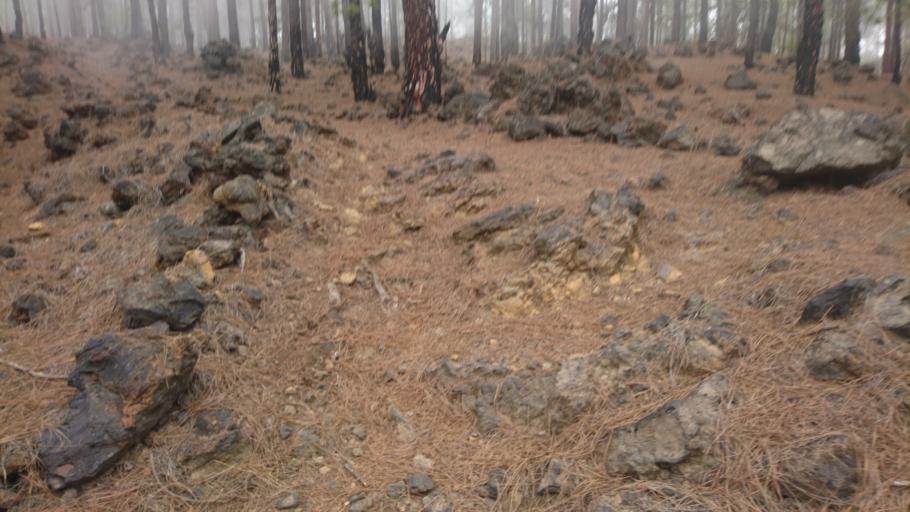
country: ES
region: Canary Islands
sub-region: Provincia de Santa Cruz de Tenerife
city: Guia de Isora
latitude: 28.2499
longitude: -16.7722
